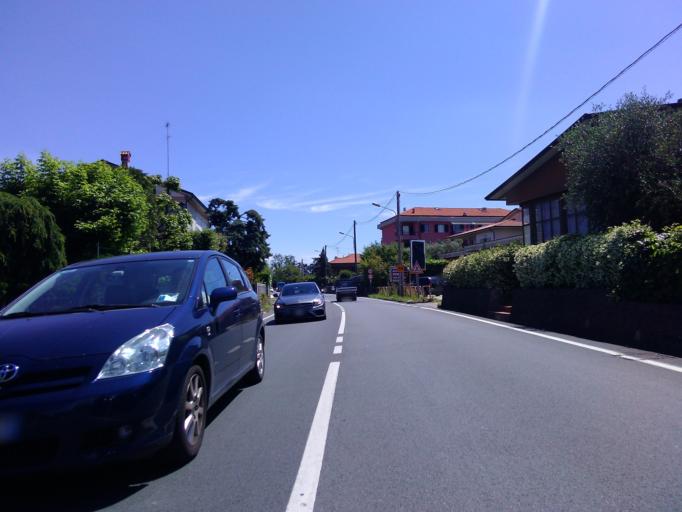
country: IT
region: Liguria
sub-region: Provincia di La Spezia
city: Santo Stefano di Magra
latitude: 44.1514
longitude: 9.9201
